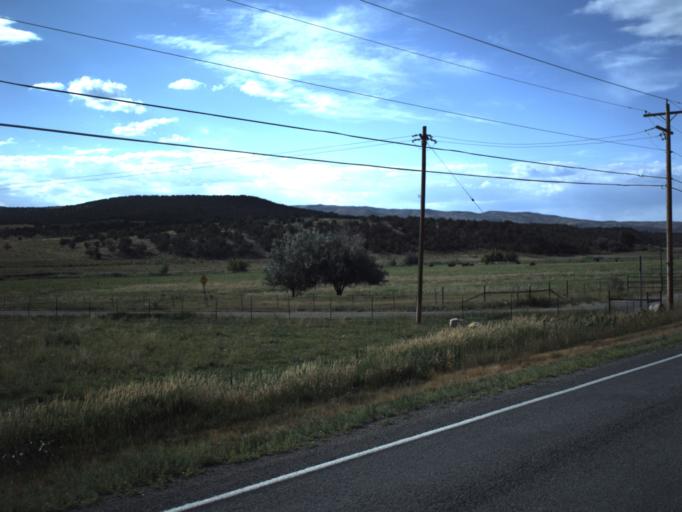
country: US
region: Utah
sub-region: Sanpete County
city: Fairview
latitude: 39.6082
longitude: -111.4447
